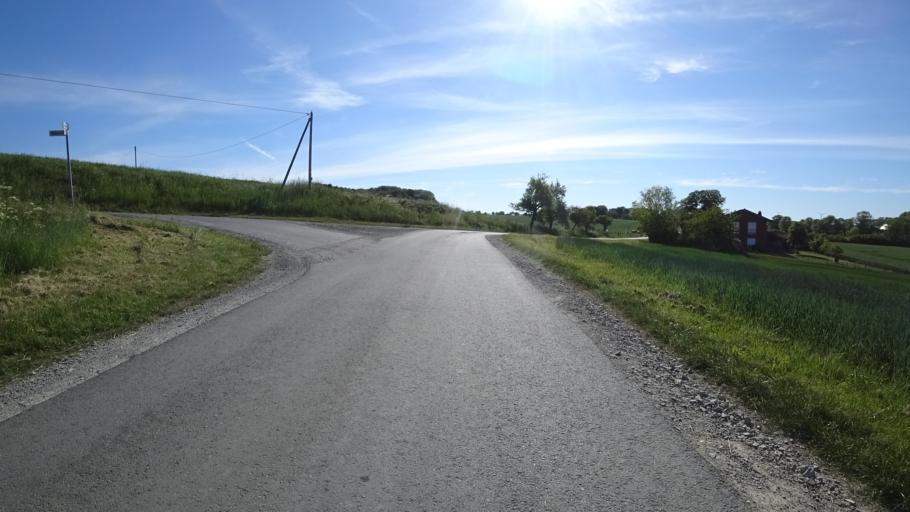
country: DE
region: North Rhine-Westphalia
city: Oelde
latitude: 51.7692
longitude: 8.1836
